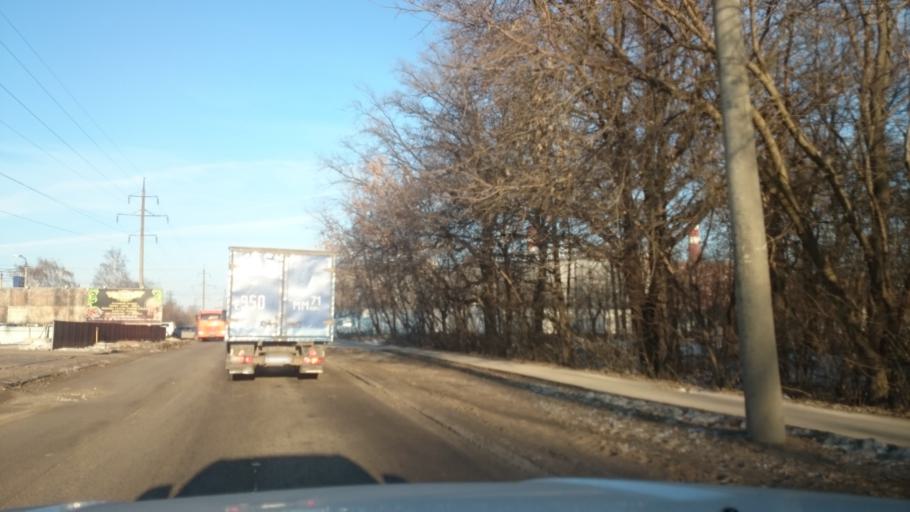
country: RU
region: Tula
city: Tula
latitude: 54.2197
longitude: 37.6848
